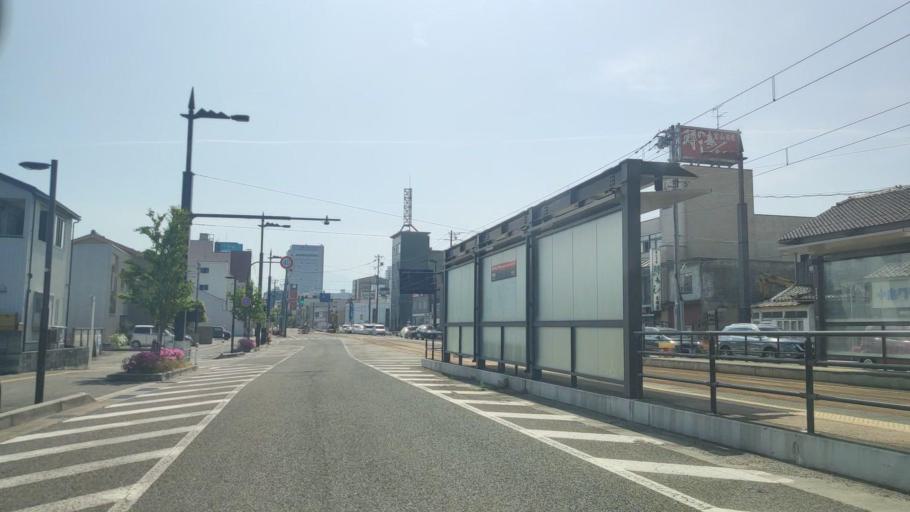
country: JP
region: Toyama
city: Toyama-shi
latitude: 36.6926
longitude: 137.2043
